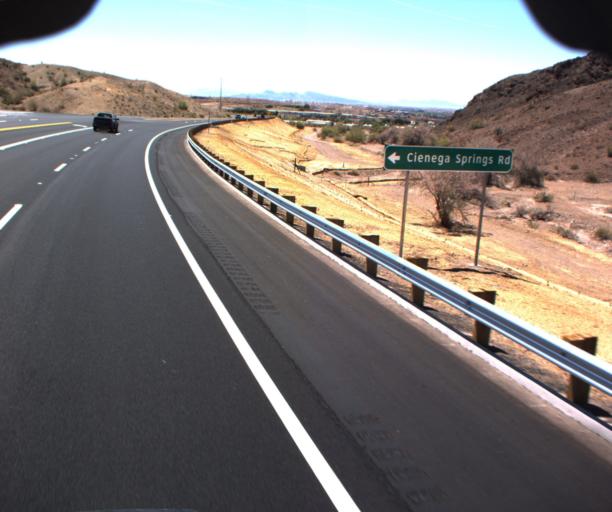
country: US
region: Arizona
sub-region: La Paz County
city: Cienega Springs
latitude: 34.1914
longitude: -114.2094
